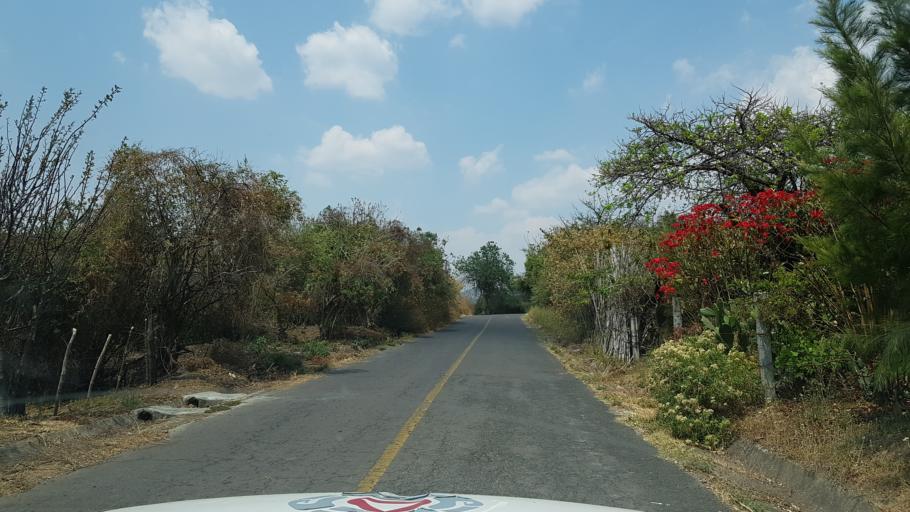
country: MX
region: Morelos
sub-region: Yecapixtla
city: Texcala
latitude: 18.9215
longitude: -98.8084
